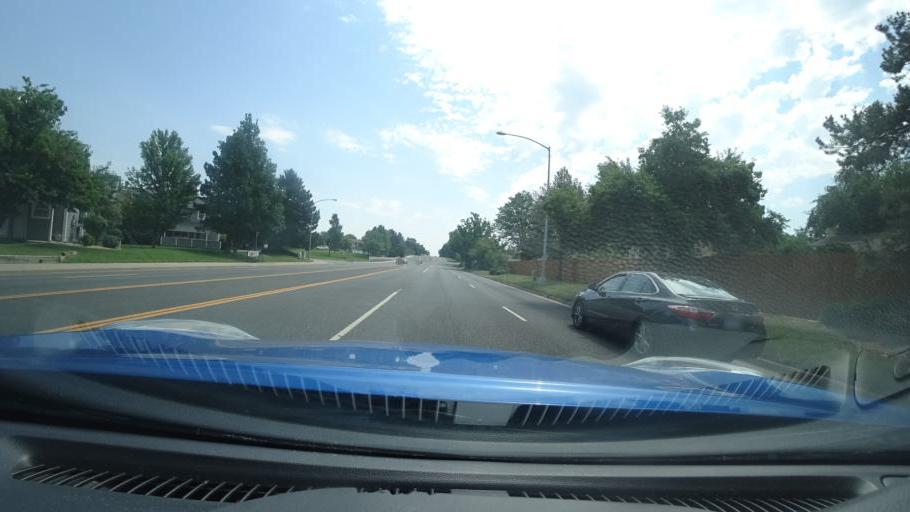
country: US
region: Colorado
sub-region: Adams County
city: Aurora
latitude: 39.6675
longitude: -104.8378
